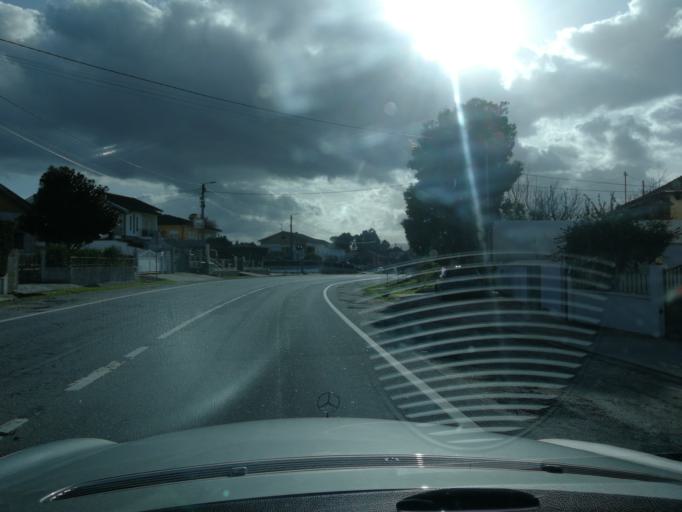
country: PT
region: Viana do Castelo
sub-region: Valenca
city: Valenza
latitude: 42.0317
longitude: -8.6300
